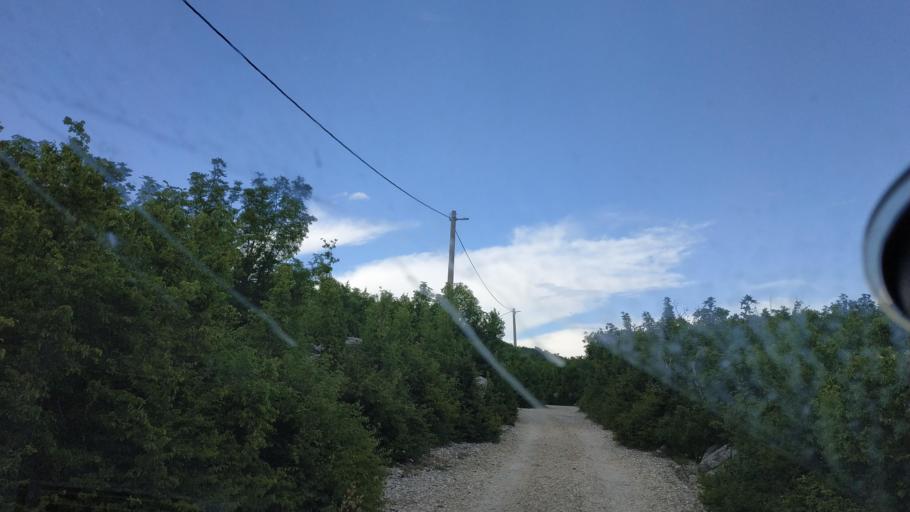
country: HR
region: Splitsko-Dalmatinska
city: Dugopolje
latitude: 43.5626
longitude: 16.6500
